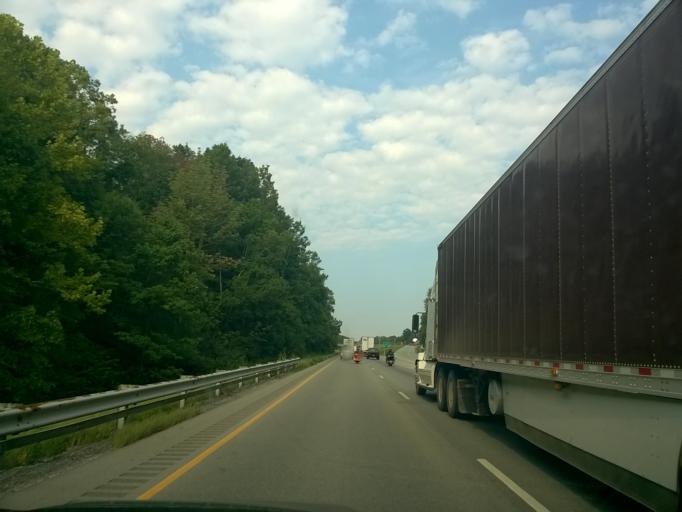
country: US
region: Indiana
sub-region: Putnam County
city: Cloverdale
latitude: 39.5246
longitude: -86.8818
